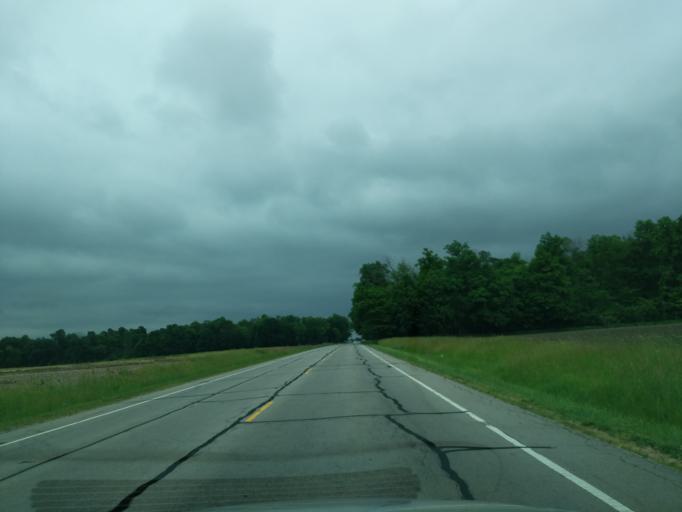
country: US
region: Indiana
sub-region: Madison County
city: Alexandria
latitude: 40.2772
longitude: -85.6065
